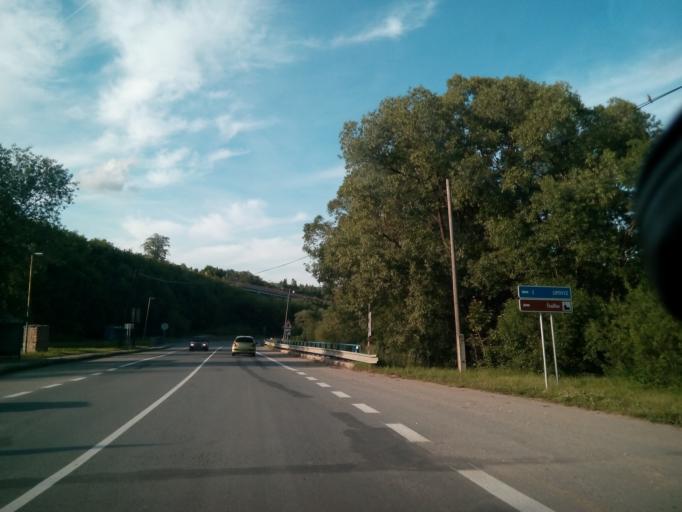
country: SK
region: Presovsky
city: Lipany
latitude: 49.0172
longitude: 20.9763
